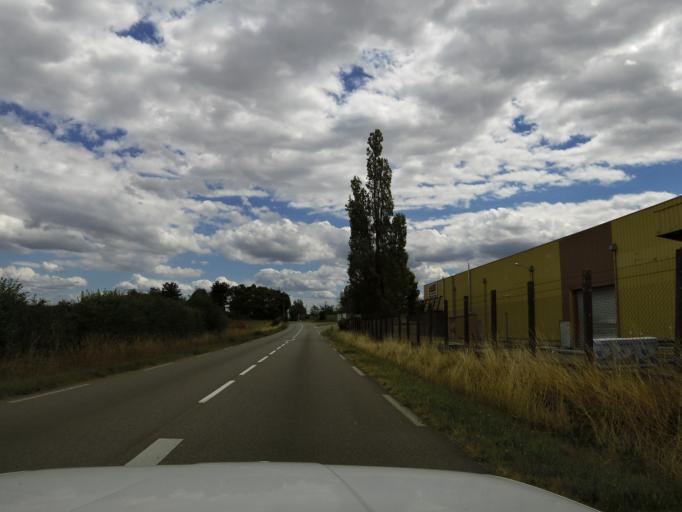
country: FR
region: Rhone-Alpes
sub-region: Departement de l'Ain
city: Meximieux
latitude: 45.8954
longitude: 5.2011
